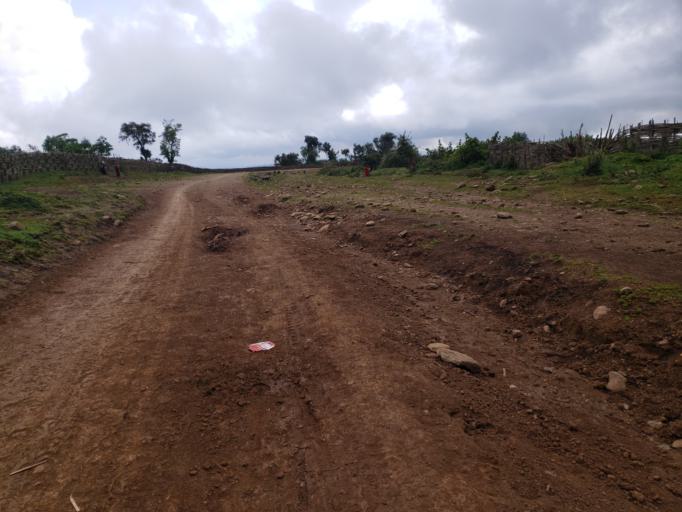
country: ET
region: Oromiya
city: Dodola
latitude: 6.7008
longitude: 39.3723
